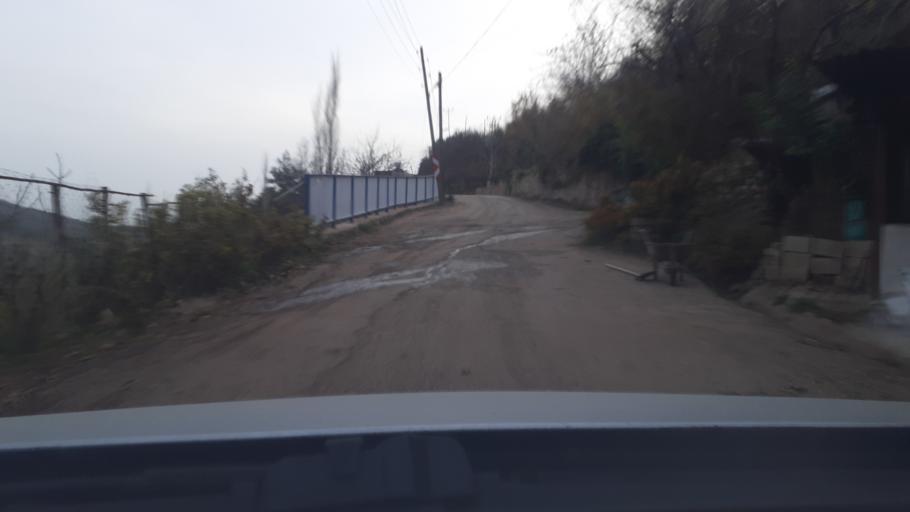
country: TR
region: Hatay
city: Kirikhan
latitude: 36.5356
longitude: 36.3143
